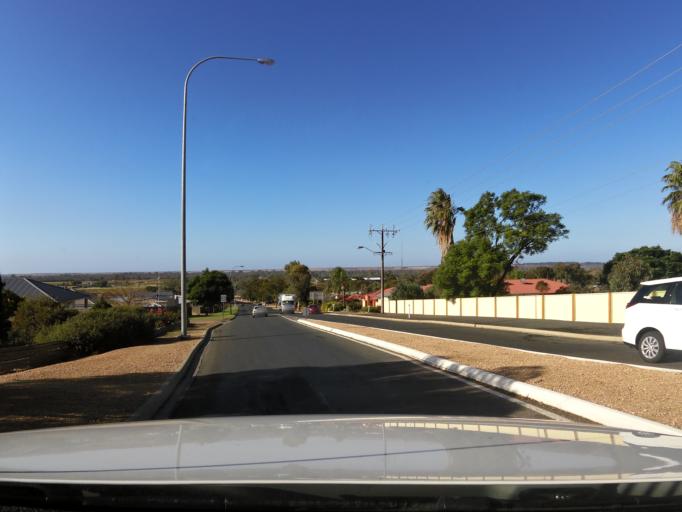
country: AU
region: South Australia
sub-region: Berri and Barmera
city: Berri
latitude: -34.2729
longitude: 140.6070
